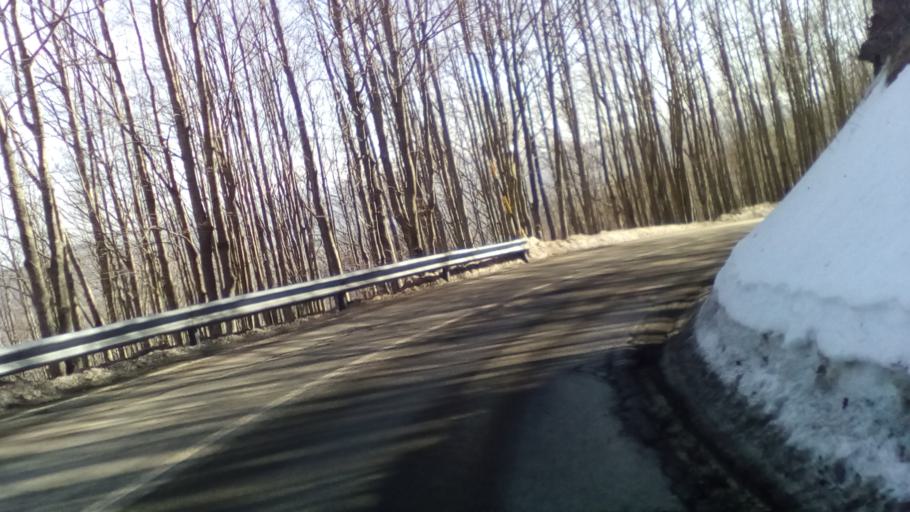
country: IT
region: Tuscany
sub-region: Provincia di Lucca
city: Fosciandora
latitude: 44.2028
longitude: 10.4970
